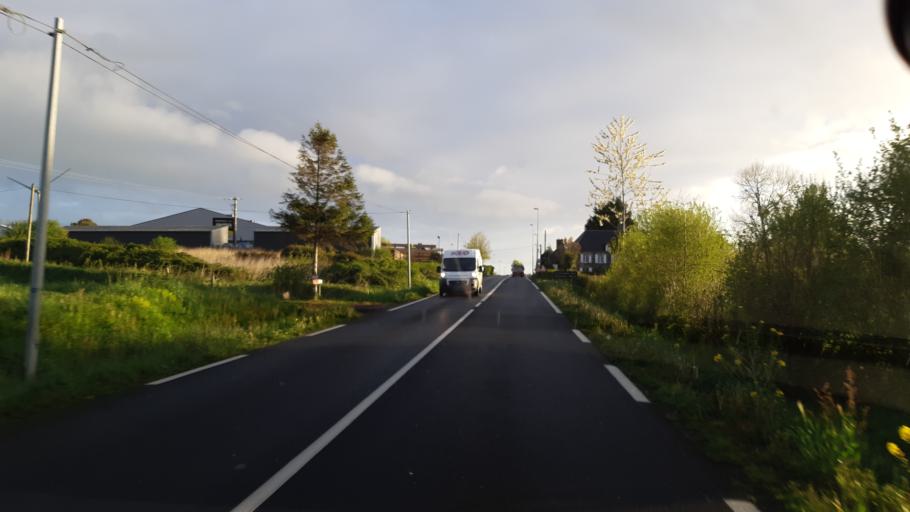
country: FR
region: Lower Normandy
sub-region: Departement de la Manche
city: Percy
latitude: 48.9951
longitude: -1.1553
